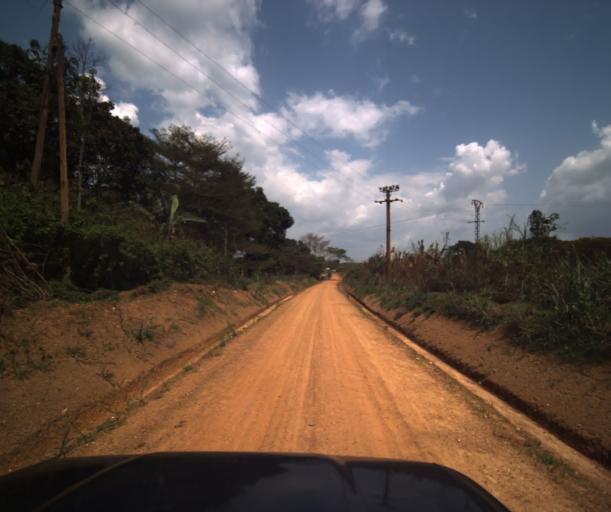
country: CM
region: Centre
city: Akono
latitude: 3.5501
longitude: 11.0541
